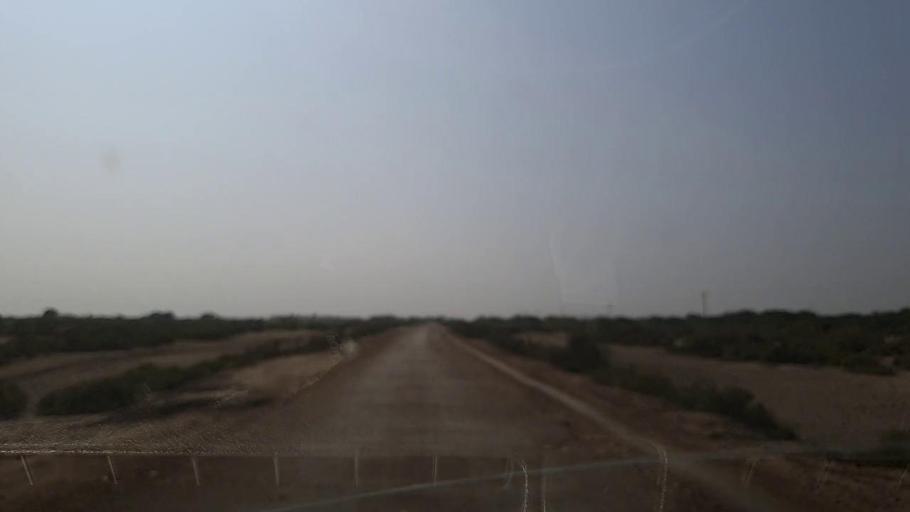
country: PK
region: Sindh
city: Mirpur Sakro
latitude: 24.5316
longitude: 67.5916
